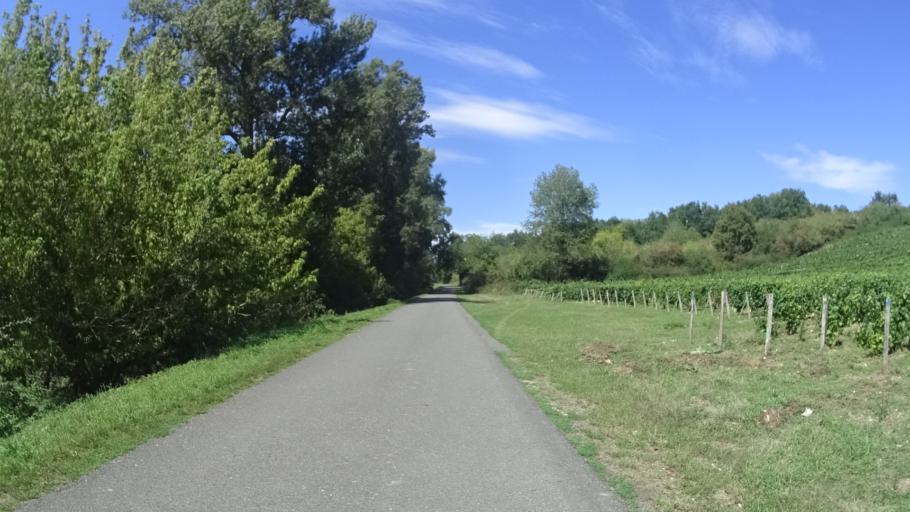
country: FR
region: Centre
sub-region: Departement du Loiret
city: Bonny-sur-Loire
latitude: 47.5816
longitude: 2.8048
